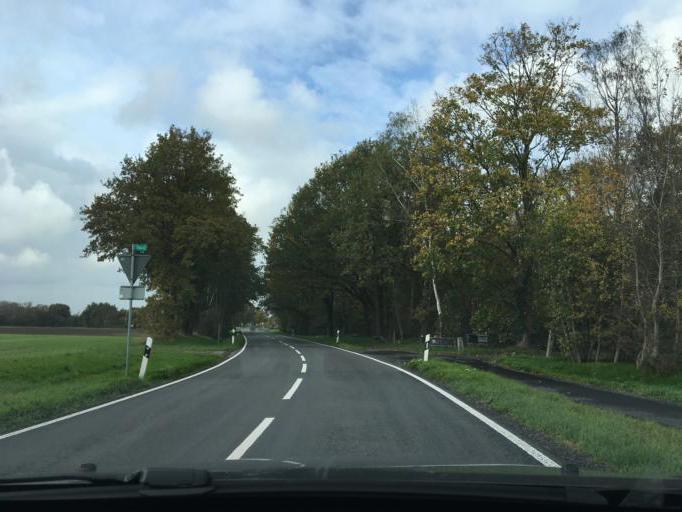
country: DE
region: North Rhine-Westphalia
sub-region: Regierungsbezirk Munster
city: Vreden
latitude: 52.0473
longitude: 6.7838
